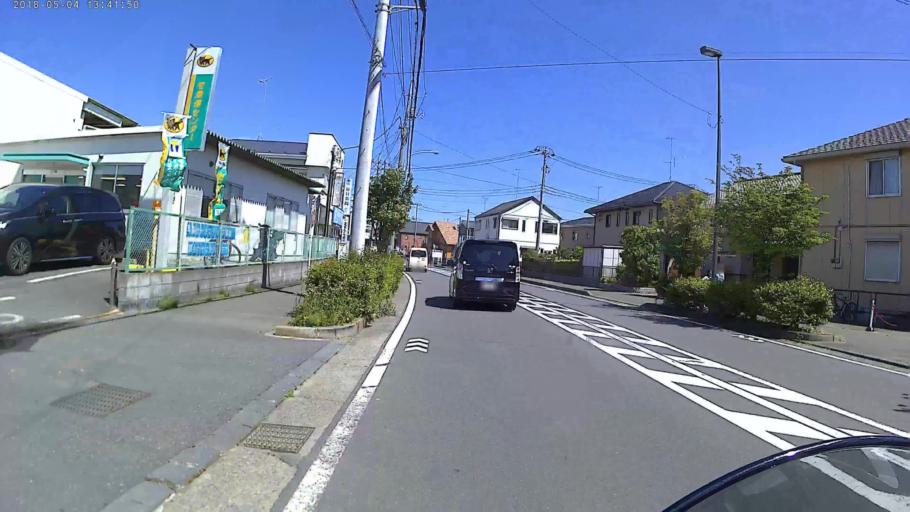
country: JP
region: Kanagawa
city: Minami-rinkan
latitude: 35.4367
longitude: 139.4626
